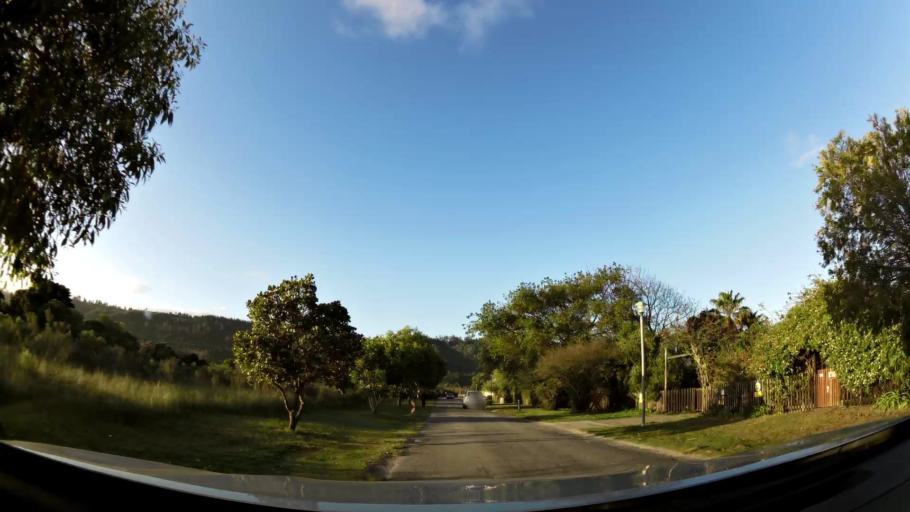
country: ZA
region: Western Cape
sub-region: Eden District Municipality
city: Knysna
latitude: -34.0156
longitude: 22.7865
